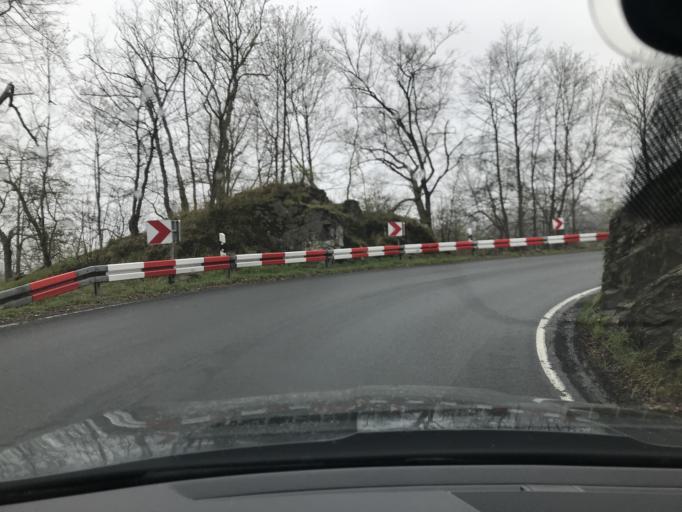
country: DE
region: Saxony-Anhalt
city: Harzgerode
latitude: 51.6651
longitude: 11.1455
